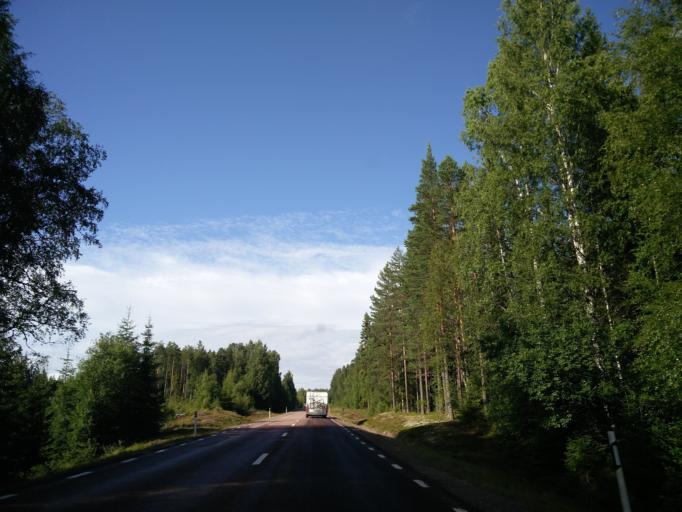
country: SE
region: Vaermland
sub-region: Hagfors Kommun
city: Ekshaerad
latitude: 60.4725
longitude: 13.3042
